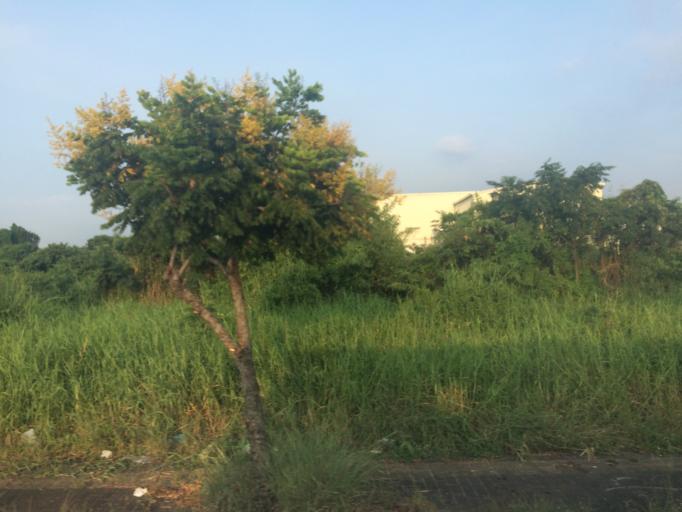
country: TW
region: Taiwan
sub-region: Chiayi
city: Jiayi Shi
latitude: 23.5275
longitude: 120.4388
